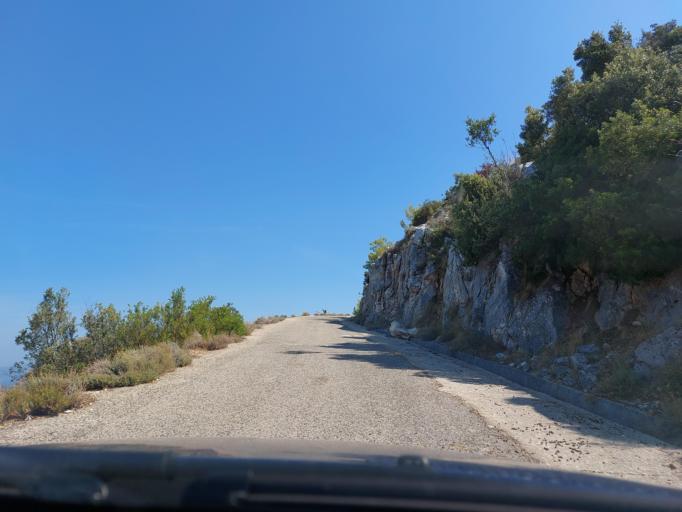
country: HR
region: Dubrovacko-Neretvanska
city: Smokvica
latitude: 42.7467
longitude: 16.8497
